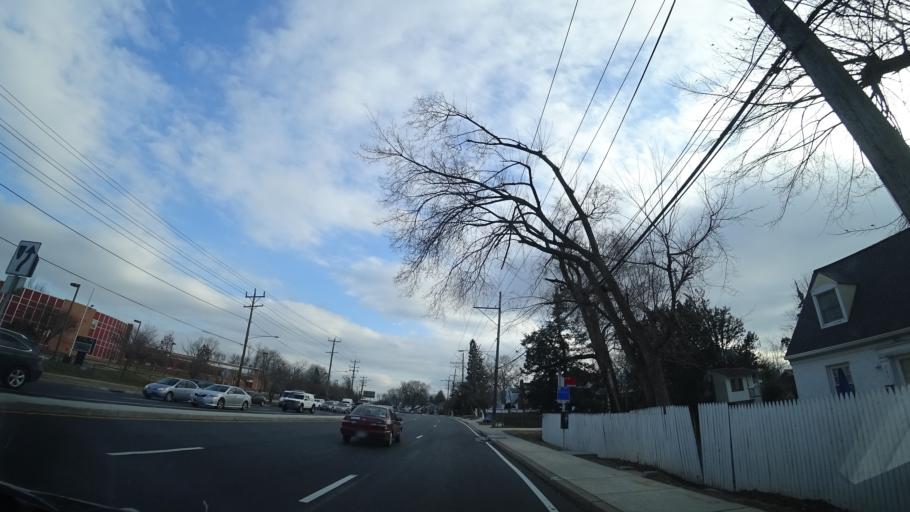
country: US
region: Maryland
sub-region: Montgomery County
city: Four Corners
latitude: 39.0122
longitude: -77.0029
